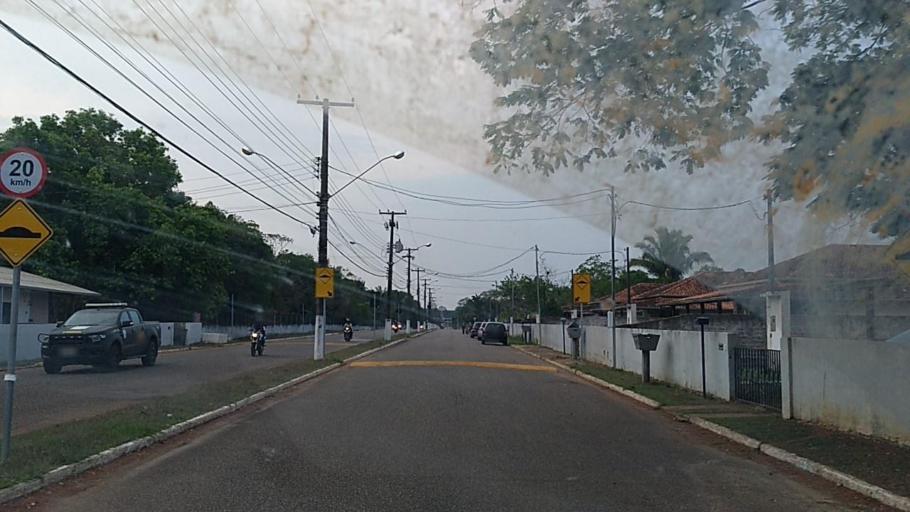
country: BR
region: Rondonia
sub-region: Porto Velho
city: Porto Velho
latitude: -8.7136
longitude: -63.8970
